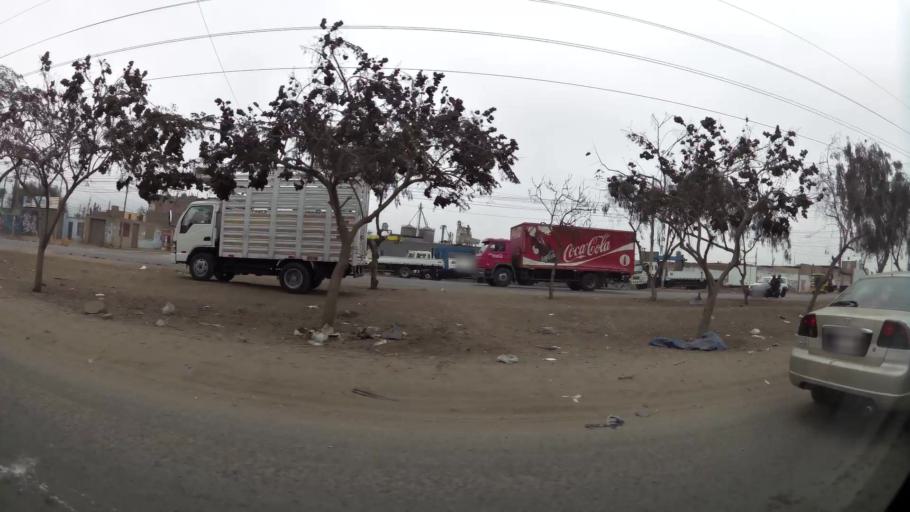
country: PE
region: Lima
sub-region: Lima
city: Independencia
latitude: -11.9302
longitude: -77.0692
